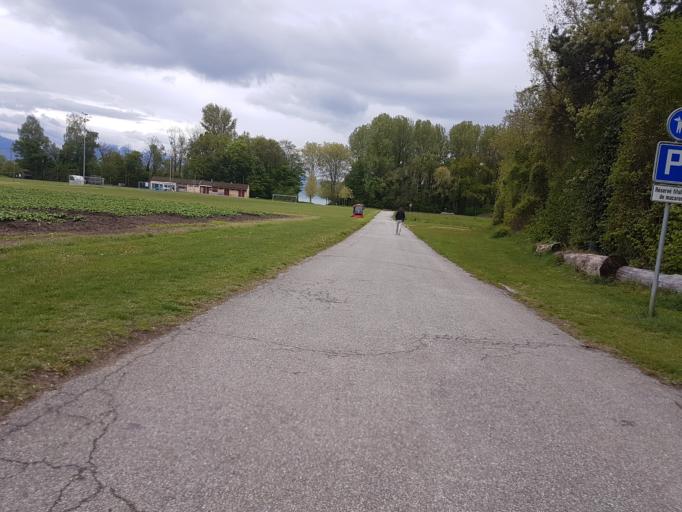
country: CH
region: Vaud
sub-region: Morges District
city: Preverenges
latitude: 46.5106
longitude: 6.5450
